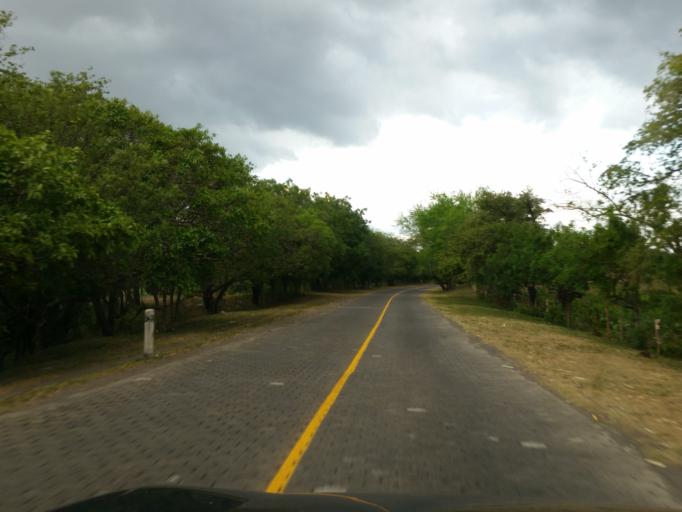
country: NI
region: Managua
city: Carlos Fonseca Amador
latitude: 12.0345
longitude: -86.5140
